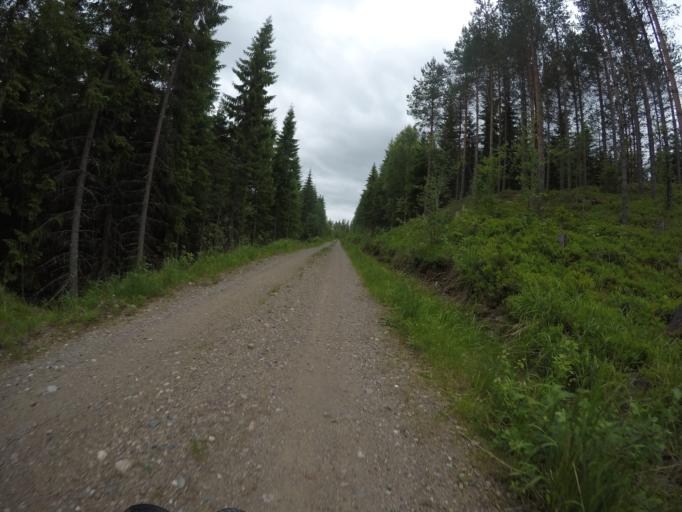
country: SE
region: Dalarna
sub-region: Ludvika Kommun
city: Abborrberget
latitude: 60.0239
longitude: 14.6026
